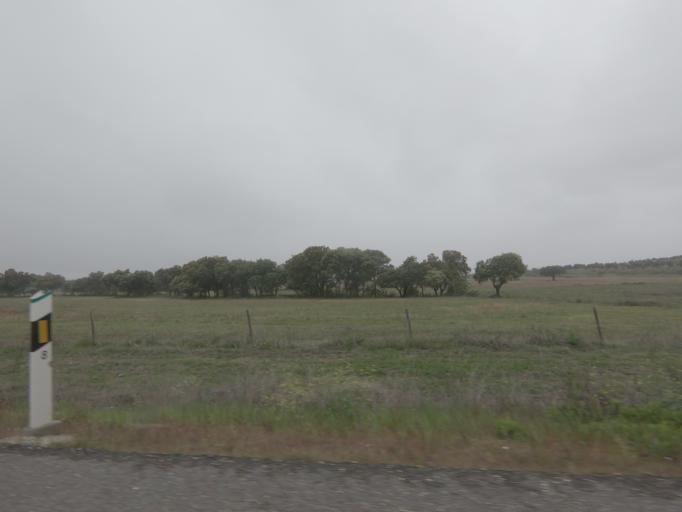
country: ES
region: Extremadura
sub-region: Provincia de Badajoz
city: La Roca de la Sierra
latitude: 39.1066
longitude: -6.7094
